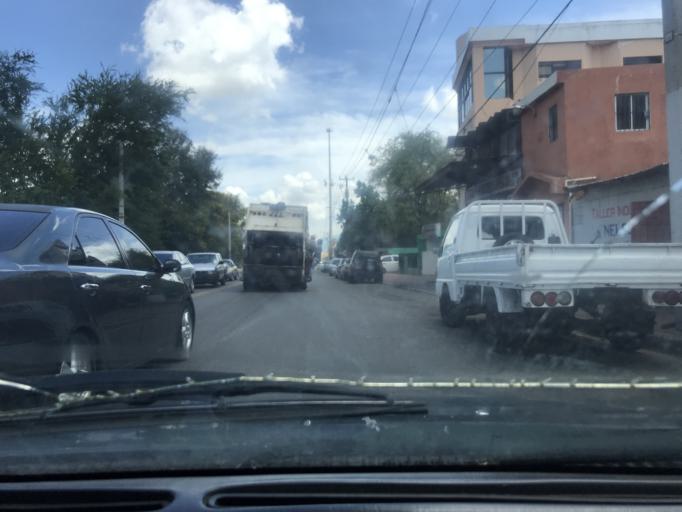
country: DO
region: Santiago
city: Santiago de los Caballeros
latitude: 19.4352
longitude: -70.6969
